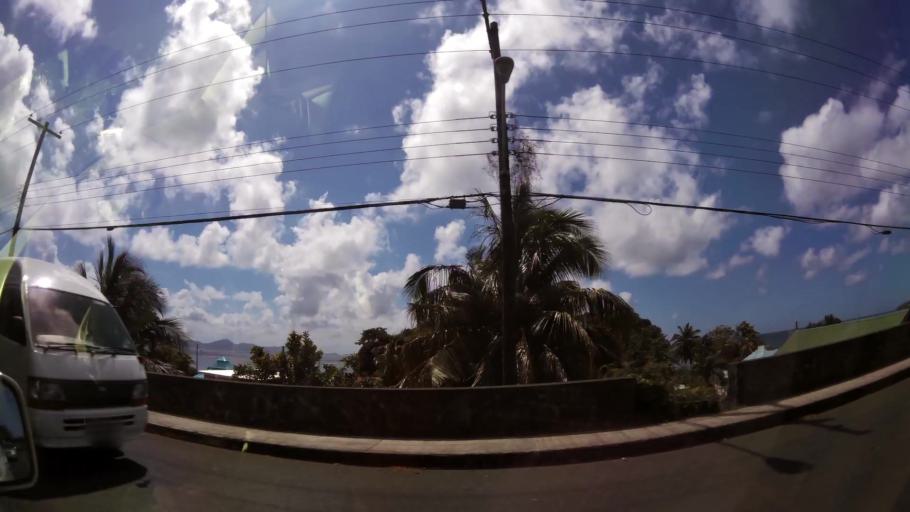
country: VC
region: Saint George
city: Kingstown
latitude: 13.1332
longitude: -61.1999
